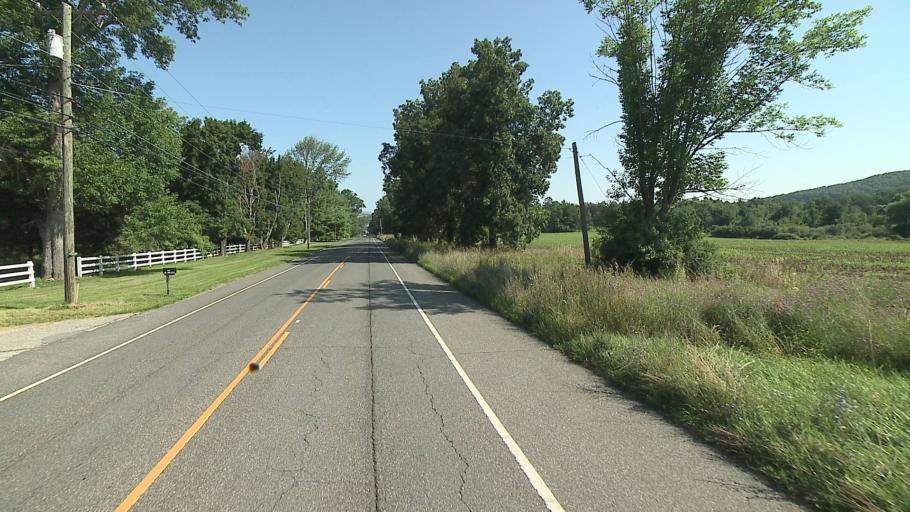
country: US
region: Connecticut
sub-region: Litchfield County
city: Canaan
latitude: 41.9067
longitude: -73.4471
